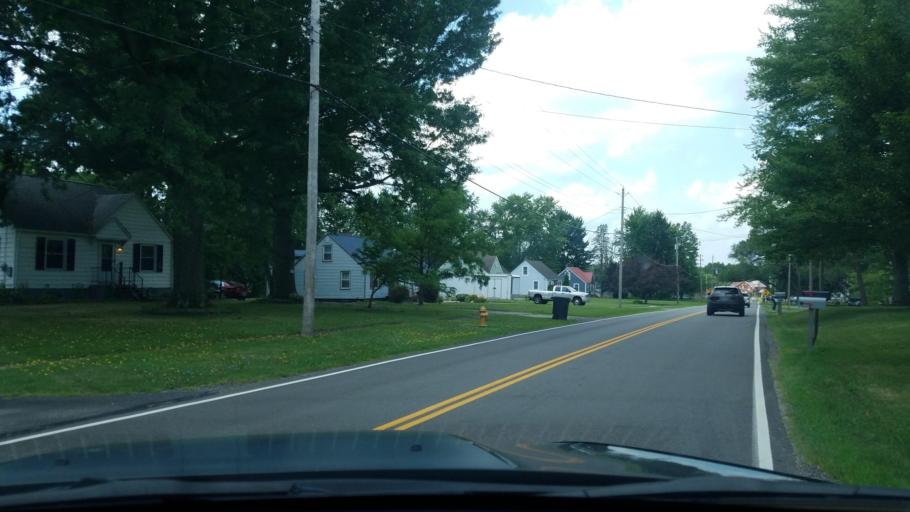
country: US
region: Ohio
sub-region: Trumbull County
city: Champion Heights
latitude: 41.2913
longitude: -80.8609
